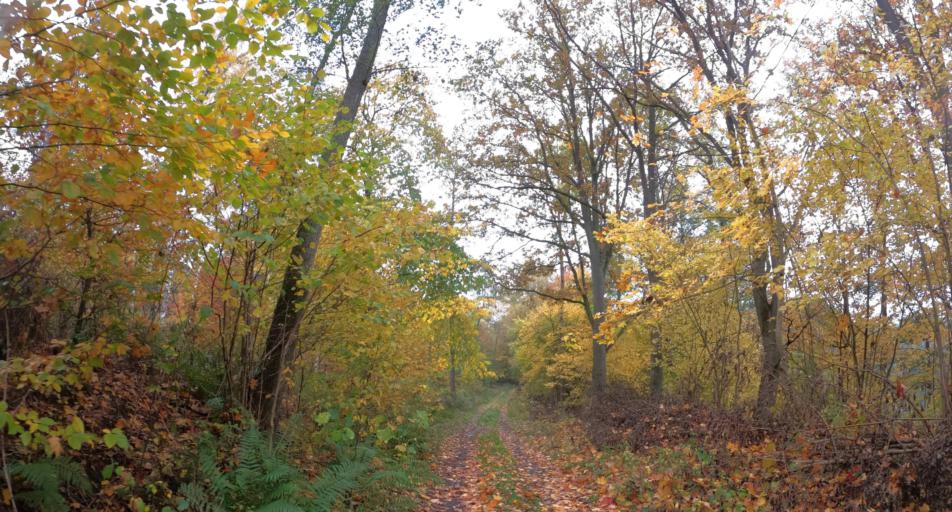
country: PL
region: West Pomeranian Voivodeship
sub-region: Powiat lobeski
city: Wegorzyno
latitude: 53.5237
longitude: 15.6678
